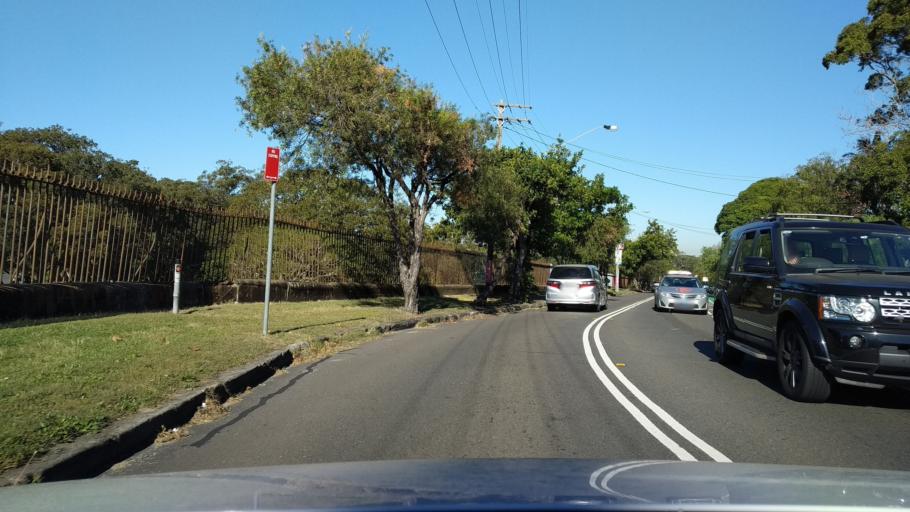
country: AU
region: New South Wales
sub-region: Woollahra
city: Woollahra
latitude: -33.8911
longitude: 151.2328
